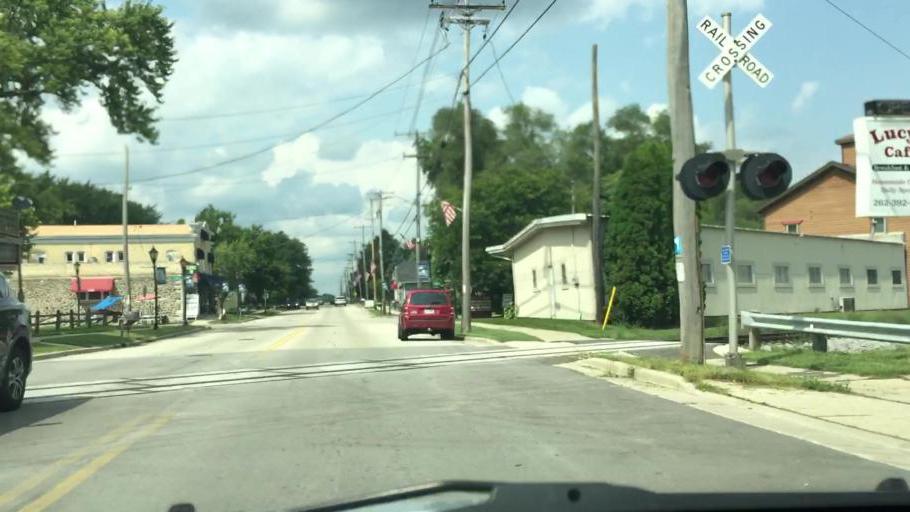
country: US
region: Wisconsin
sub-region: Waukesha County
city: North Prairie
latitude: 42.9345
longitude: -88.4056
